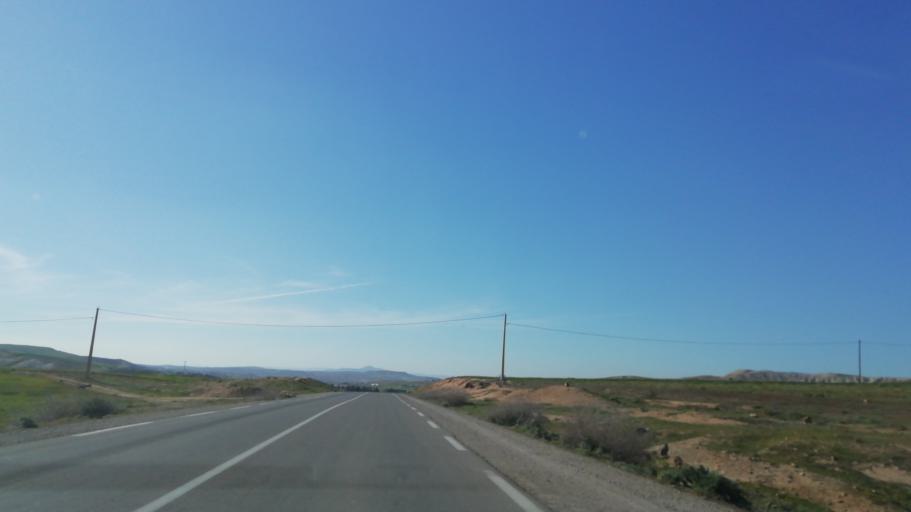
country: DZ
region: Mascara
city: Oued el Abtal
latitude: 35.4547
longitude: 0.7680
